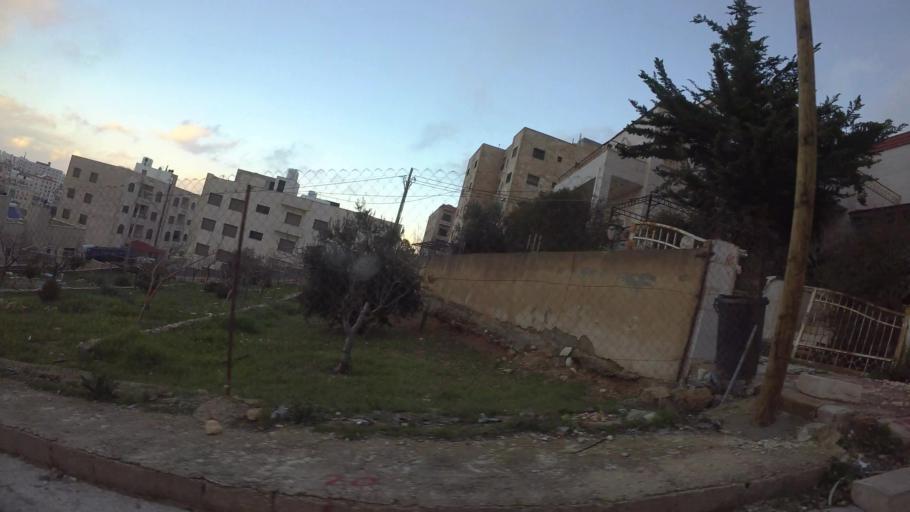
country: JO
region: Amman
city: Al Jubayhah
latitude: 32.0503
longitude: 35.8934
